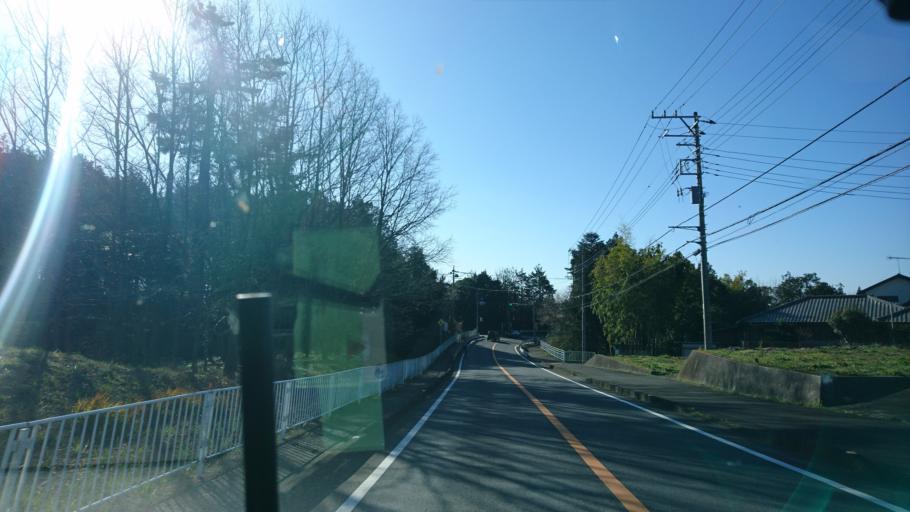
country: JP
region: Shizuoka
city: Fujinomiya
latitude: 35.2877
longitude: 138.6028
